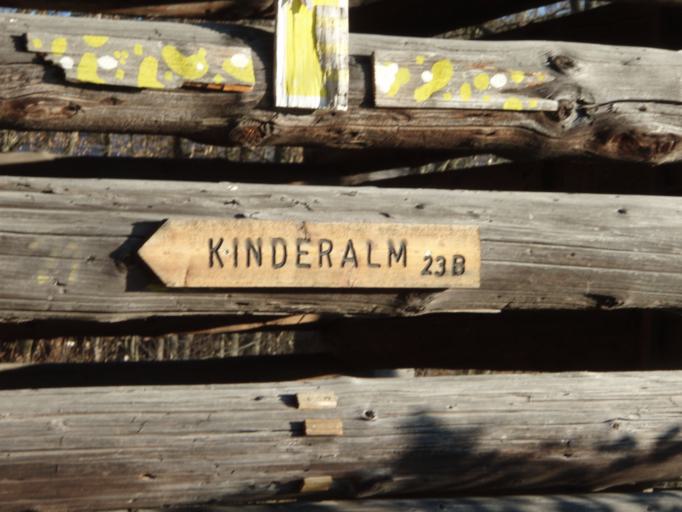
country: AT
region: Salzburg
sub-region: Politischer Bezirk Sankt Johann im Pongau
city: Sankt Veit im Pongau
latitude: 47.3321
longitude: 13.1605
